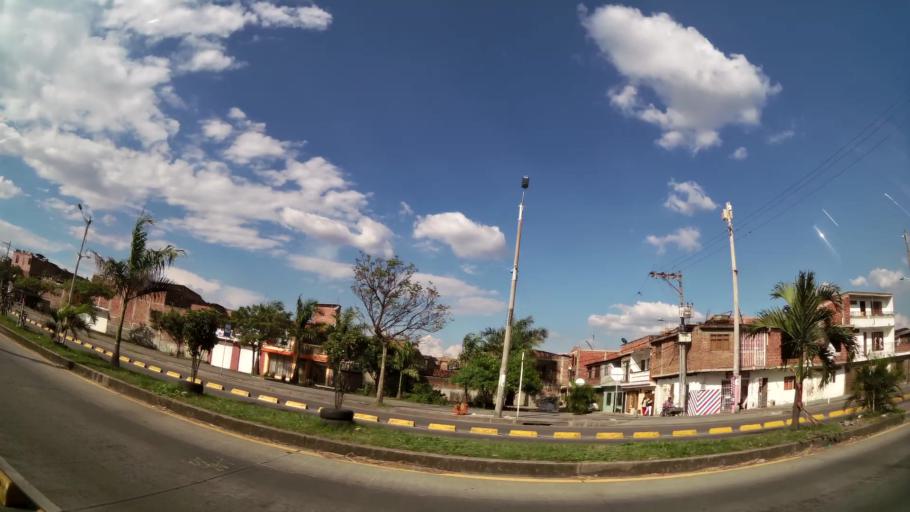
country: CO
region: Valle del Cauca
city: Cali
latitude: 3.4206
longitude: -76.4896
